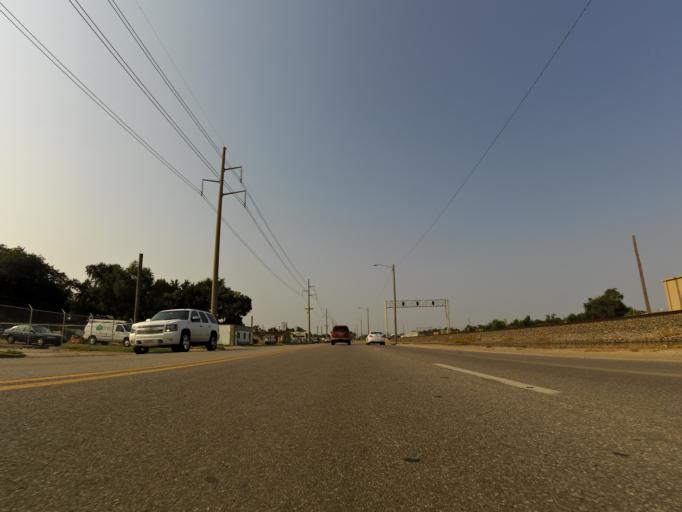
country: US
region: Kansas
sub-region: Sedgwick County
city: Wichita
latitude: 37.7461
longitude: -97.3360
